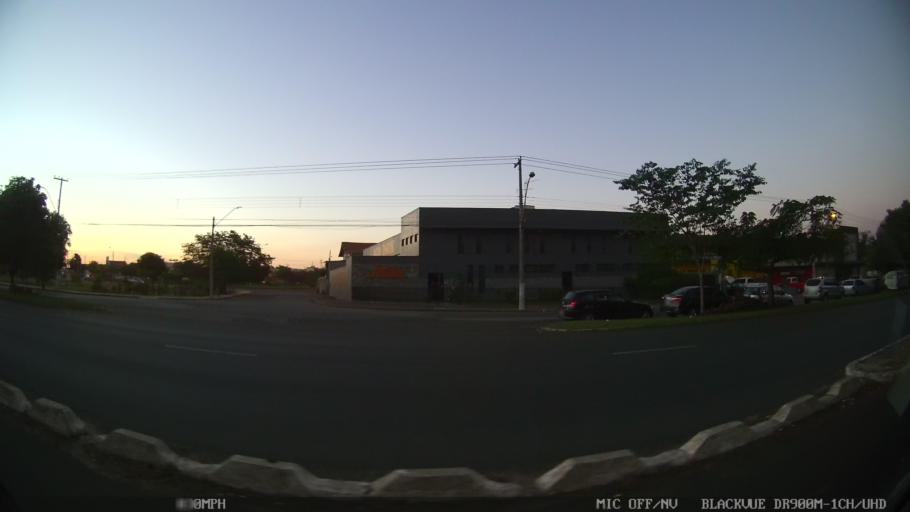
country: BR
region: Sao Paulo
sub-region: Americana
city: Americana
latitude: -22.7446
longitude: -47.3523
